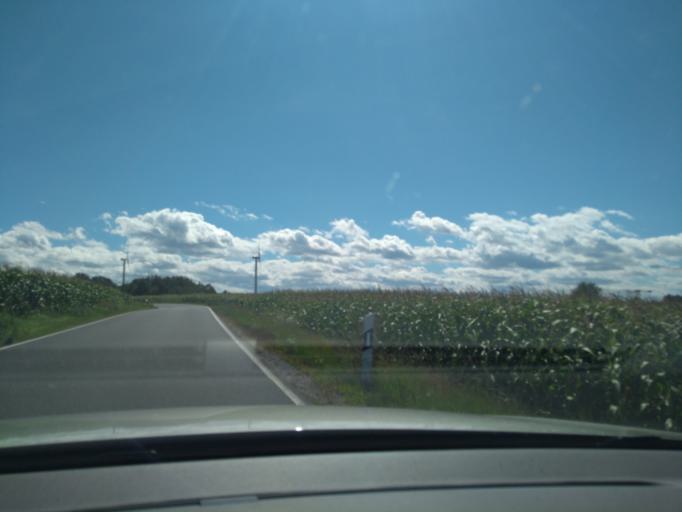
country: DE
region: Saxony
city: Lichtenberg
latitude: 51.1411
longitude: 13.9556
